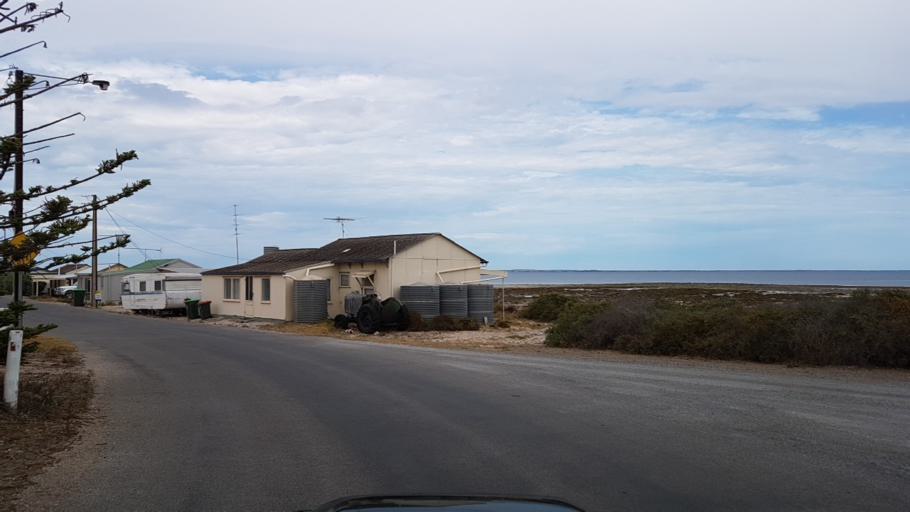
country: AU
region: South Australia
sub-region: Yorke Peninsula
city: Honiton
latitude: -34.8919
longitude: 137.4566
